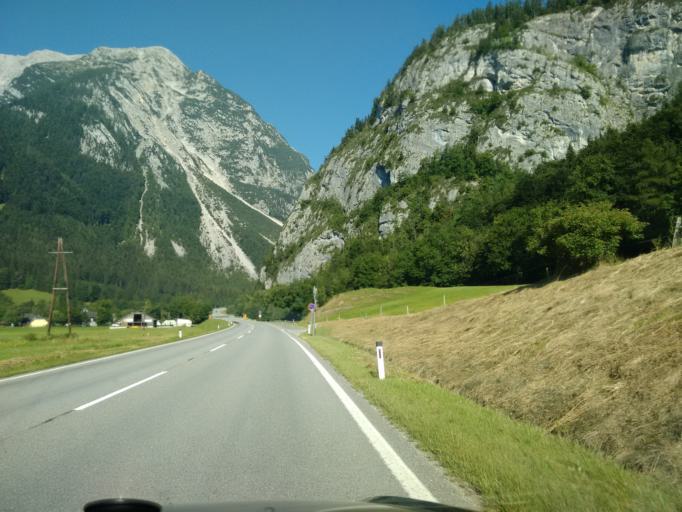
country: AT
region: Styria
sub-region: Politischer Bezirk Liezen
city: Irdning
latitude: 47.5264
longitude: 14.0667
